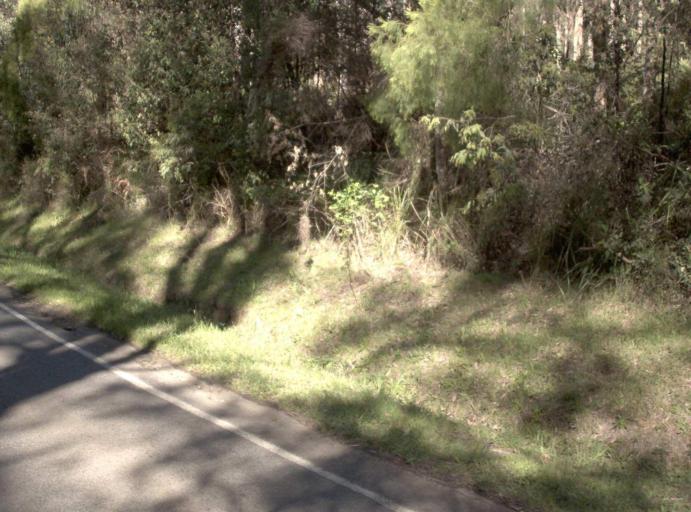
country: AU
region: Victoria
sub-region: Yarra Ranges
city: Millgrove
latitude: -37.8817
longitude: 145.8618
